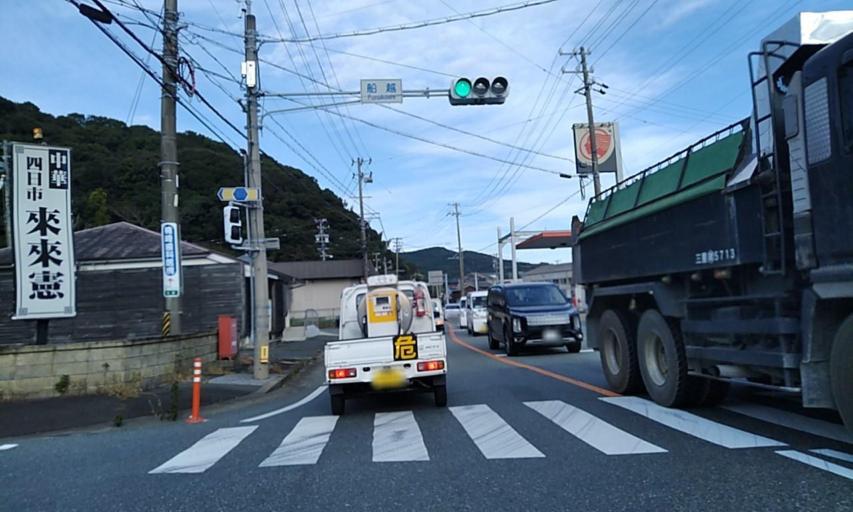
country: JP
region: Mie
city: Ise
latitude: 34.3475
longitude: 136.6898
